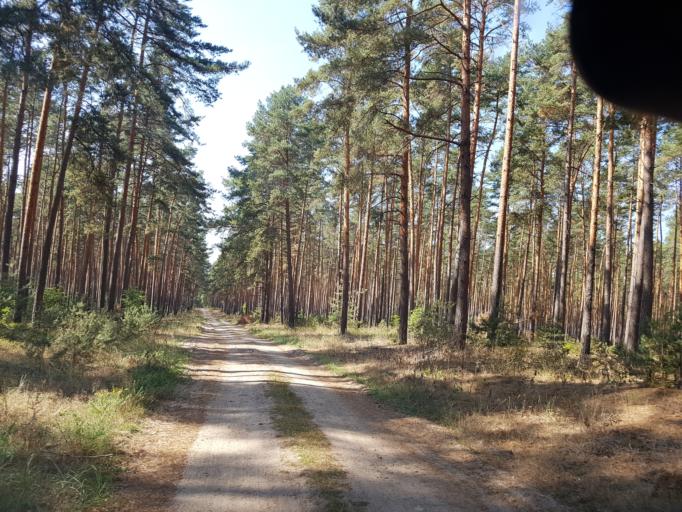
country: DE
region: Brandenburg
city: Gorzke
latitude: 52.0746
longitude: 12.3390
